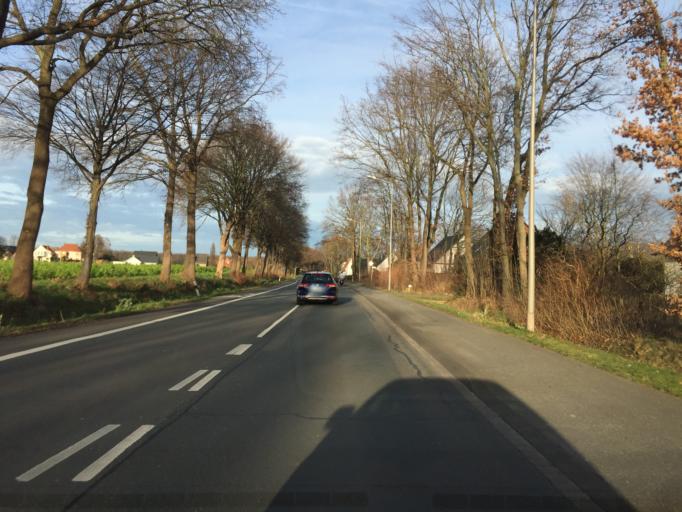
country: DE
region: North Rhine-Westphalia
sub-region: Regierungsbezirk Detmold
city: Minden
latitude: 52.3224
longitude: 8.9204
